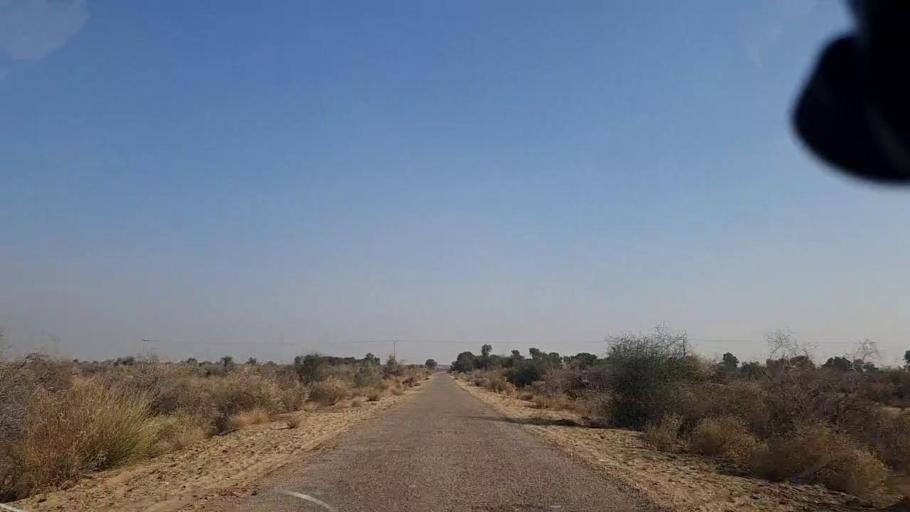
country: PK
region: Sindh
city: Khanpur
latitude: 27.6448
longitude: 69.5970
